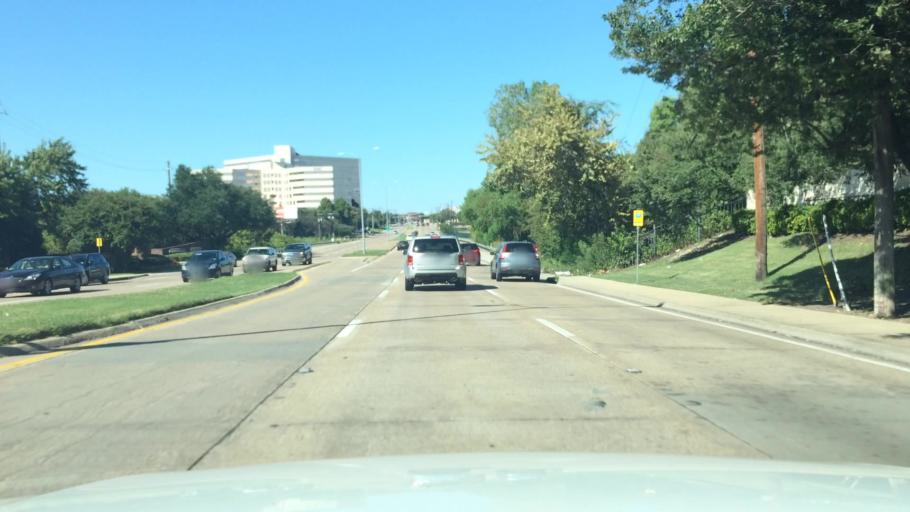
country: US
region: Texas
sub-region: Dallas County
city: Addison
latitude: 32.9444
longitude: -96.8035
